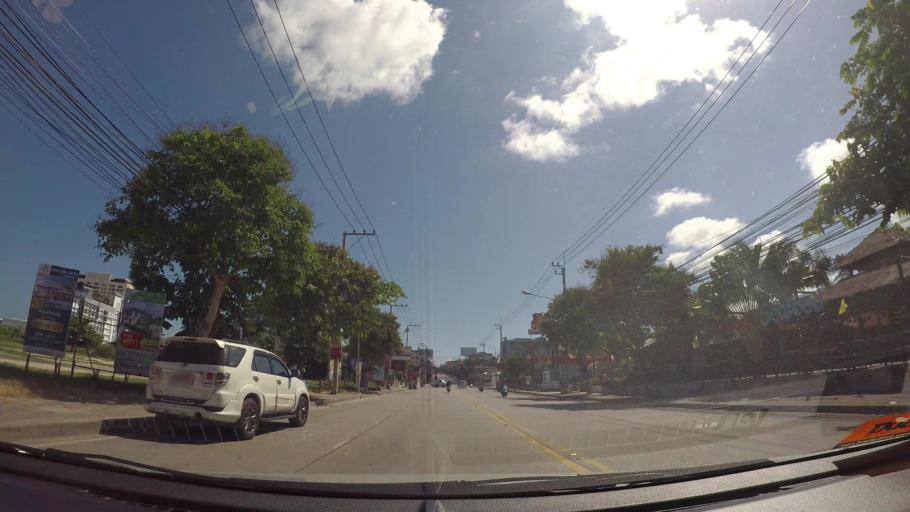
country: TH
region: Chon Buri
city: Phatthaya
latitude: 12.9410
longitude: 100.8944
